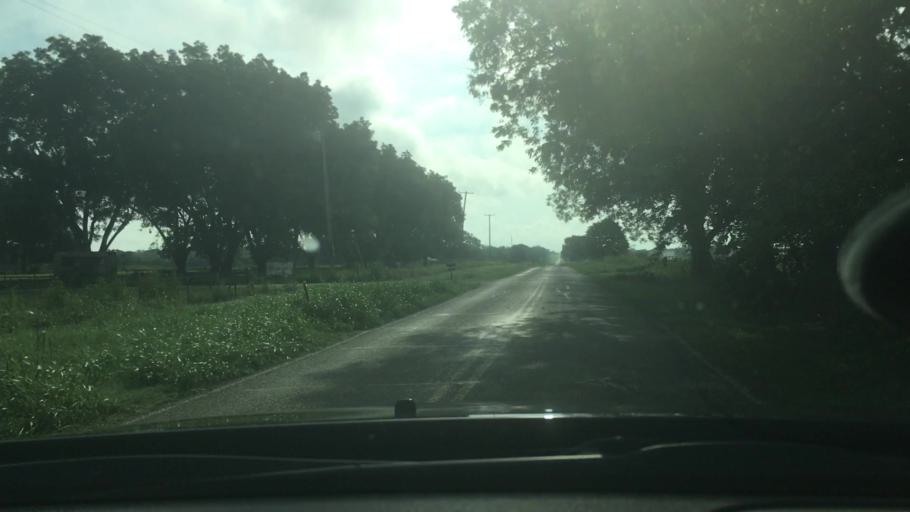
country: US
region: Oklahoma
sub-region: Pontotoc County
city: Ada
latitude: 34.6945
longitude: -96.5541
